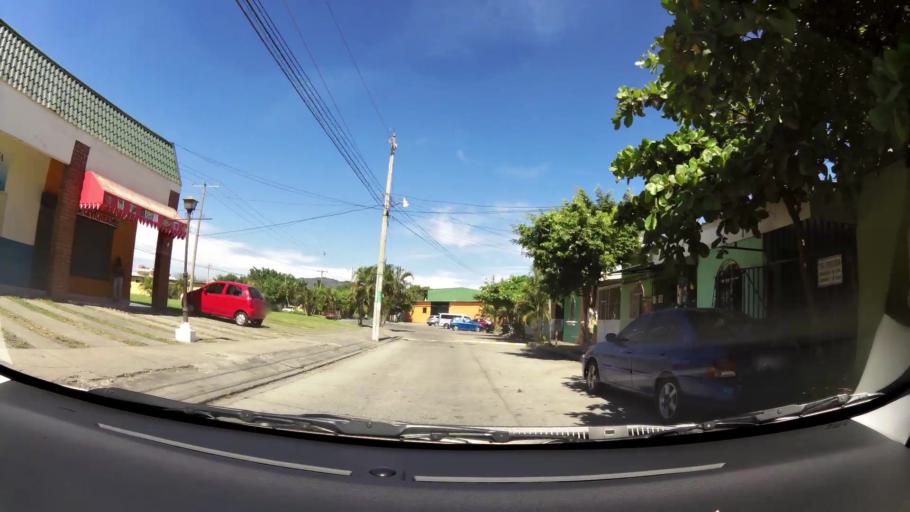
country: SV
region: La Libertad
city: San Juan Opico
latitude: 13.7942
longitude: -89.3595
